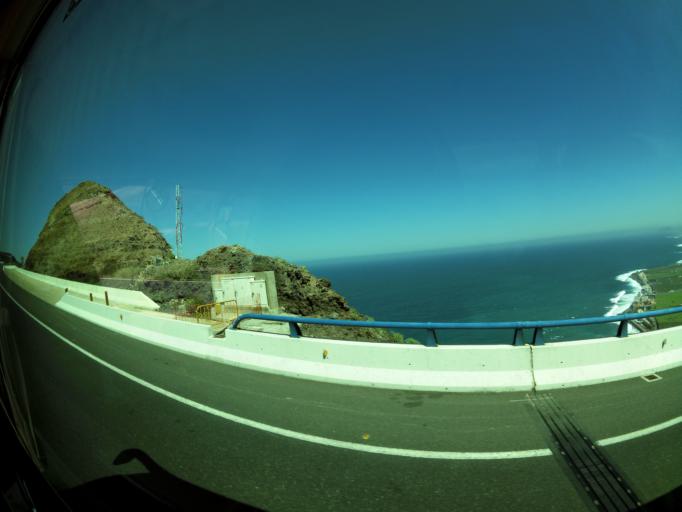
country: ES
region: Canary Islands
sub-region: Provincia de Las Palmas
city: Guia
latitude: 28.1427
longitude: -15.6034
